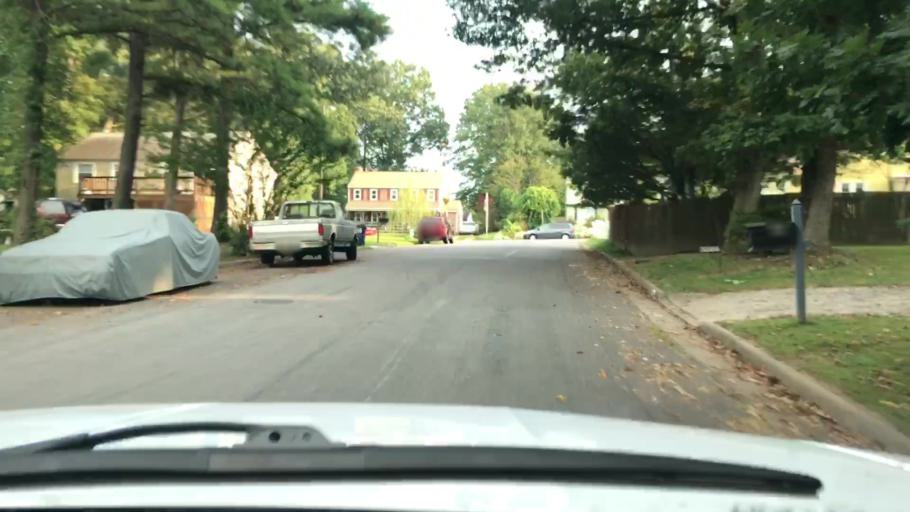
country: US
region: Virginia
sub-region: Chesterfield County
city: Chesterfield
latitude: 37.4402
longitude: -77.5154
